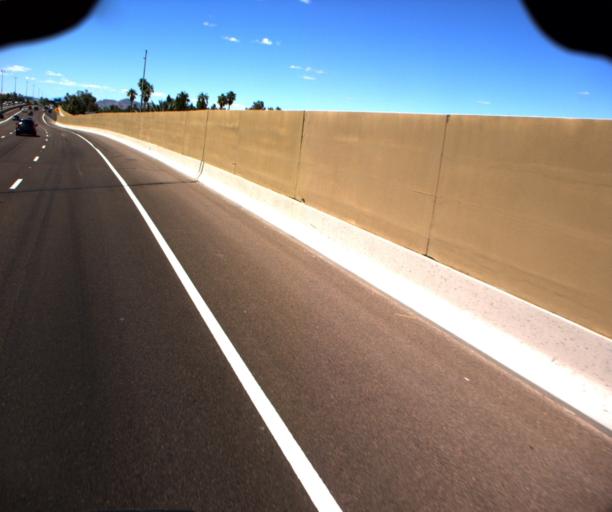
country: US
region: Arizona
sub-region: Maricopa County
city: Phoenix
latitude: 33.4827
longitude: -112.0391
